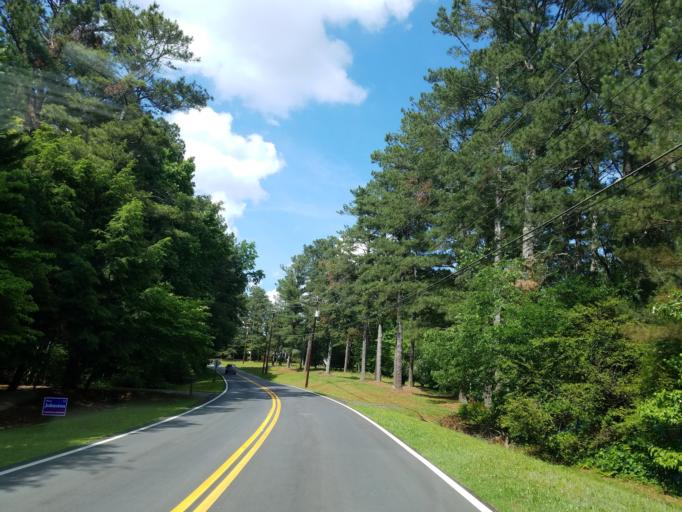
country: US
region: Georgia
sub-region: Cherokee County
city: Holly Springs
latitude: 34.1709
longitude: -84.5116
